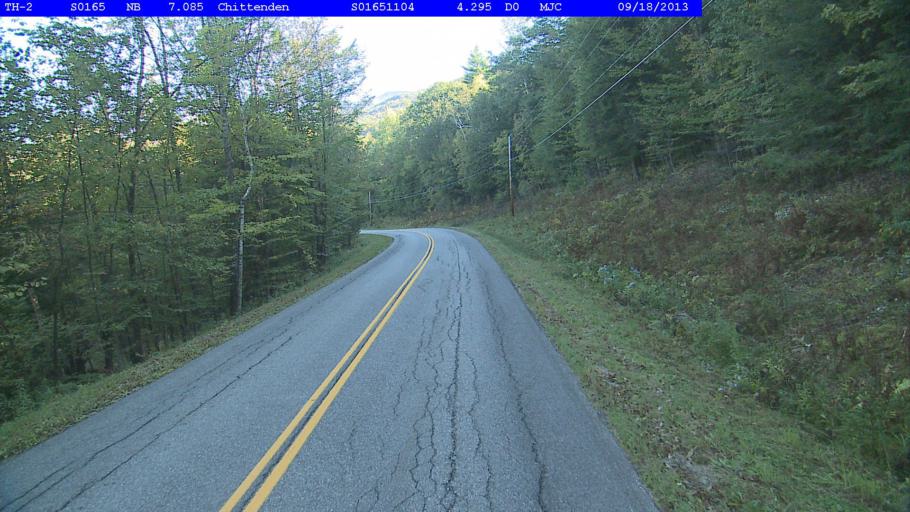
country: US
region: Vermont
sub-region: Rutland County
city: Rutland
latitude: 43.7358
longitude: -72.9712
